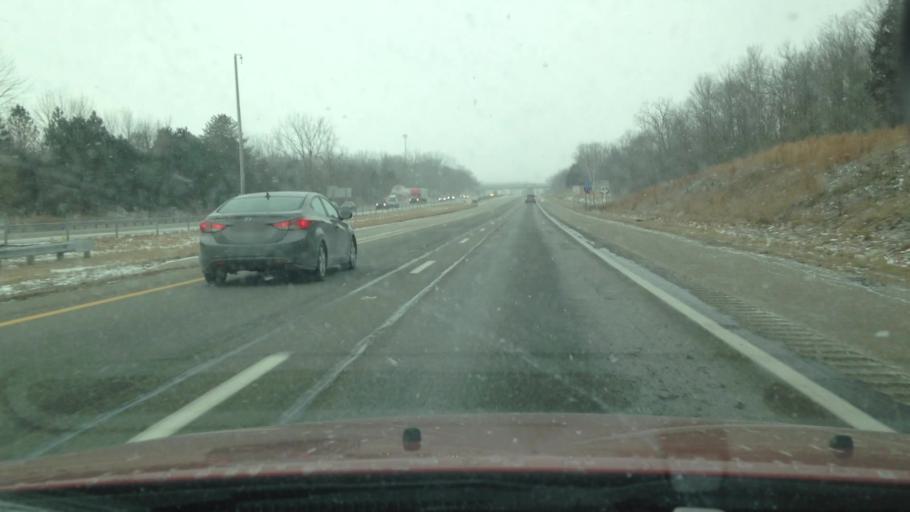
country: US
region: Ohio
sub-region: Montgomery County
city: Clayton
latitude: 39.8542
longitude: -84.3500
